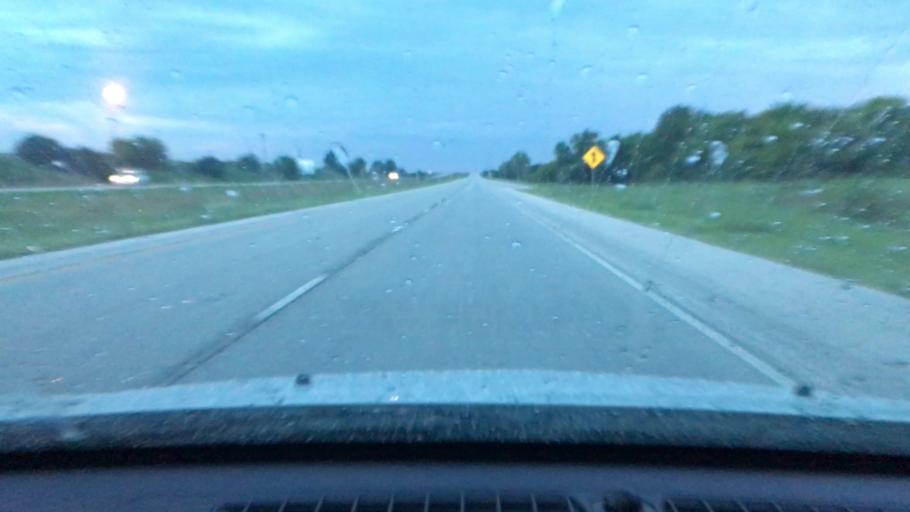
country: US
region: Illinois
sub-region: Morgan County
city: South Jacksonville
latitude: 39.7214
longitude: -90.1699
